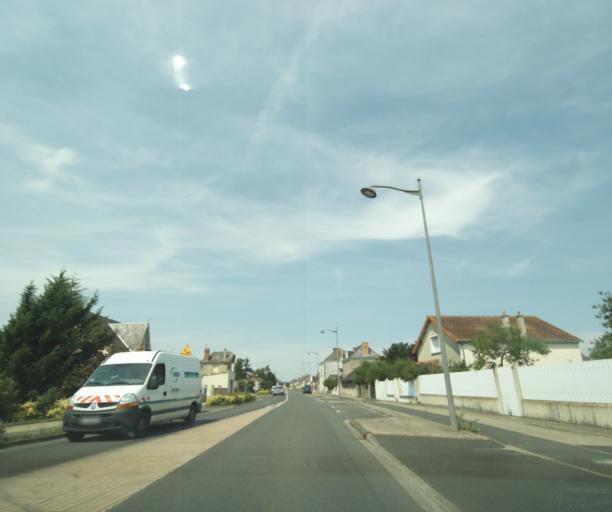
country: FR
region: Poitou-Charentes
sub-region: Departement de la Vienne
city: Dange-Saint-Romain
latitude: 46.9319
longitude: 0.6048
